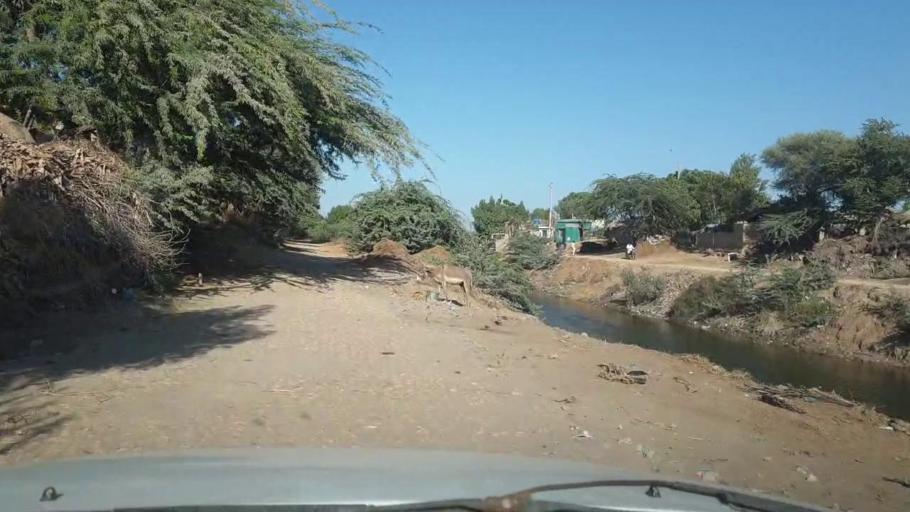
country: PK
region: Sindh
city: Thatta
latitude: 24.5538
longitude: 67.8430
